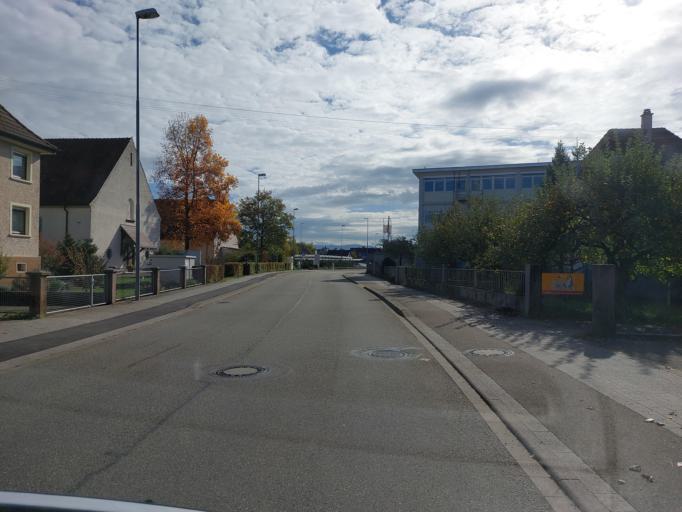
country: DE
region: Baden-Wuerttemberg
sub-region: Freiburg Region
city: Teningen
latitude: 48.1334
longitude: 7.8066
